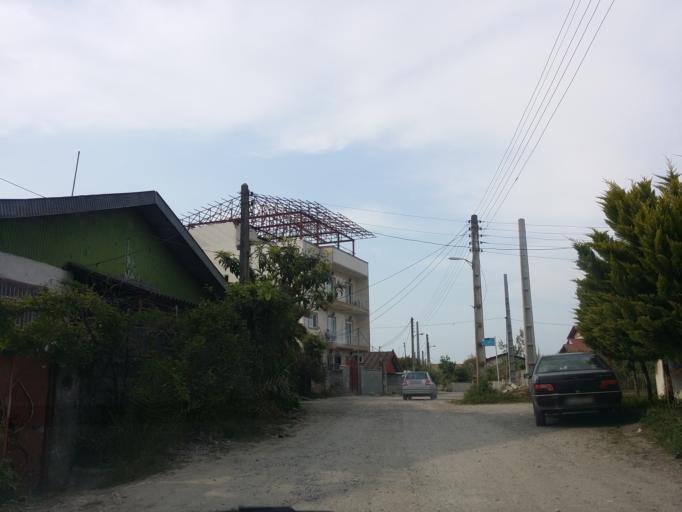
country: IR
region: Mazandaran
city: Chalus
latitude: 36.6782
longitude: 51.3932
